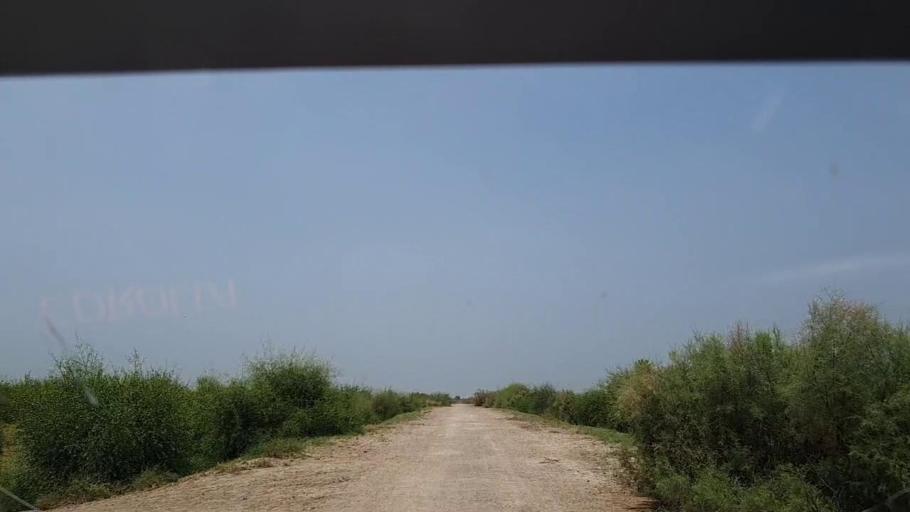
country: PK
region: Sindh
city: Adilpur
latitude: 27.8949
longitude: 69.2429
